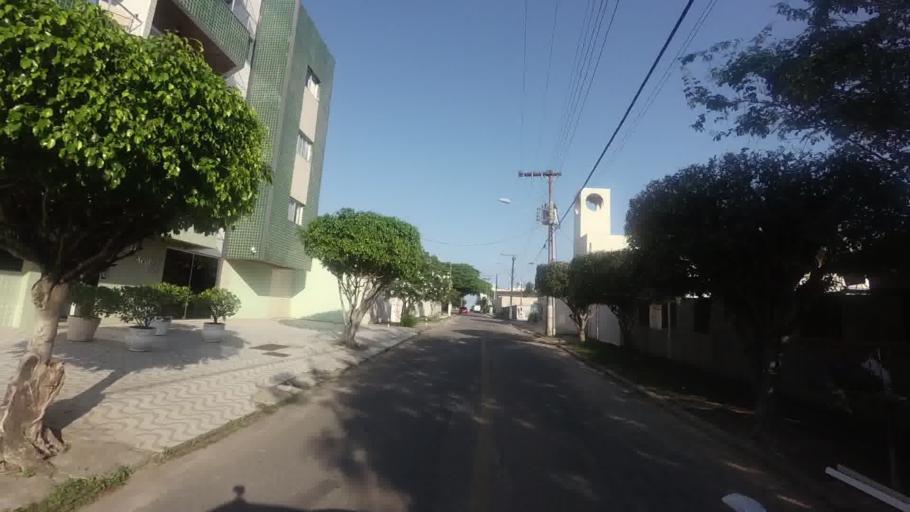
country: BR
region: Espirito Santo
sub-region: Guarapari
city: Guarapari
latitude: -20.7277
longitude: -40.5311
